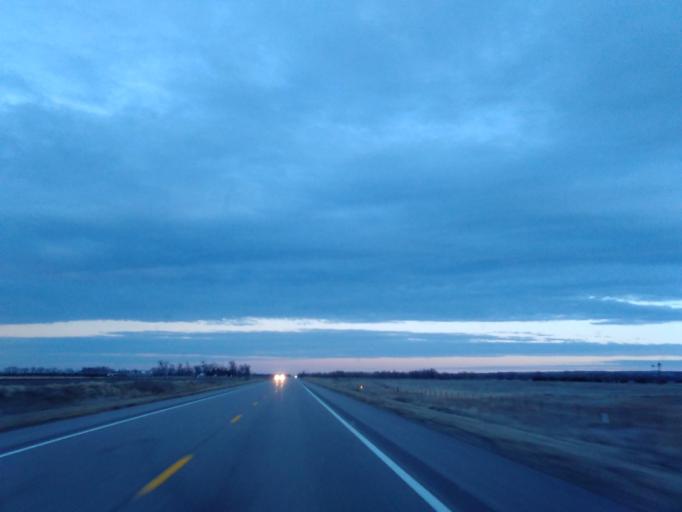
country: US
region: Nebraska
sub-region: Garden County
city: Oshkosh
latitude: 41.3692
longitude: -102.2403
